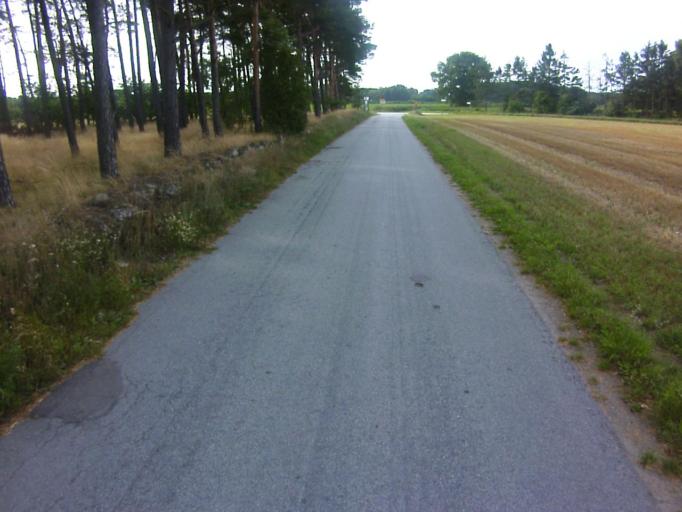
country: SE
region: Blekinge
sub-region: Solvesborgs Kommun
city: Soelvesborg
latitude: 56.0271
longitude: 14.7126
